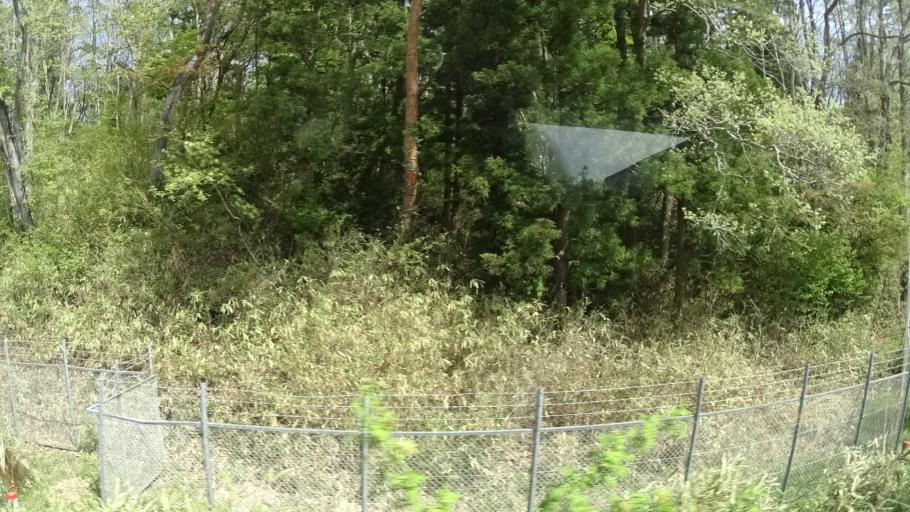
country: JP
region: Fukushima
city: Namie
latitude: 37.6175
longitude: 140.9874
